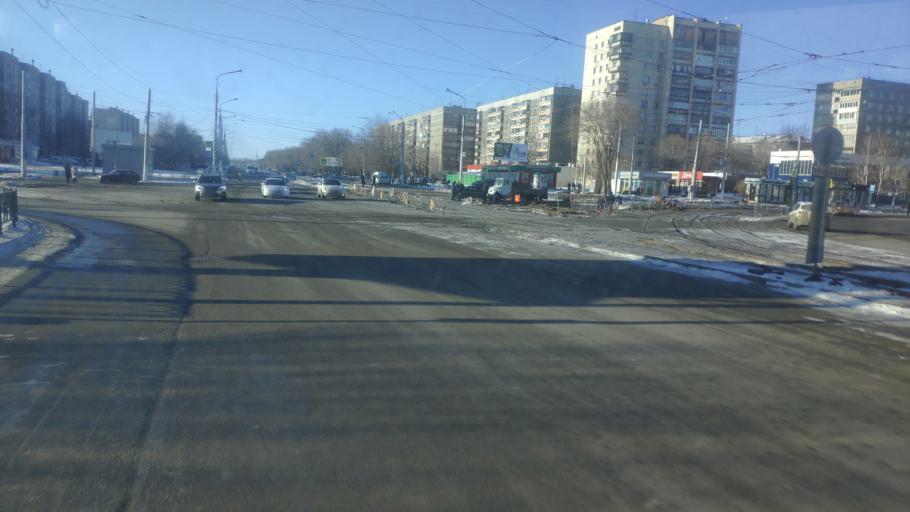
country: RU
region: Chelyabinsk
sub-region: Gorod Magnitogorsk
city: Magnitogorsk
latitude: 53.3648
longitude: 58.9792
